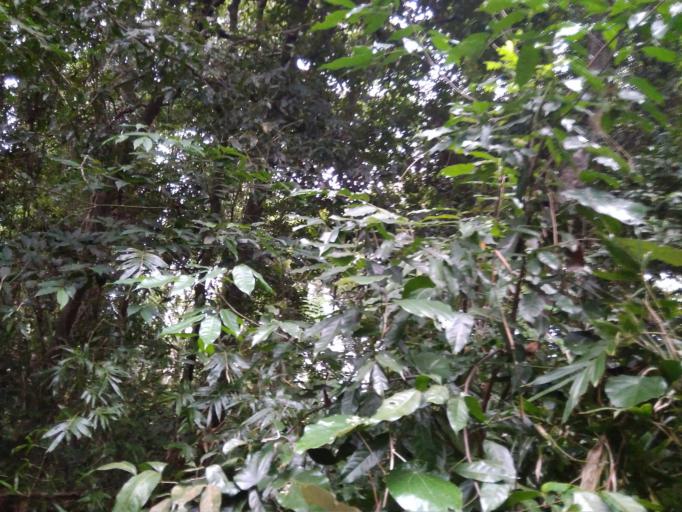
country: TH
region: Krabi
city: Ko Lanta
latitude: 7.4719
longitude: 99.1014
